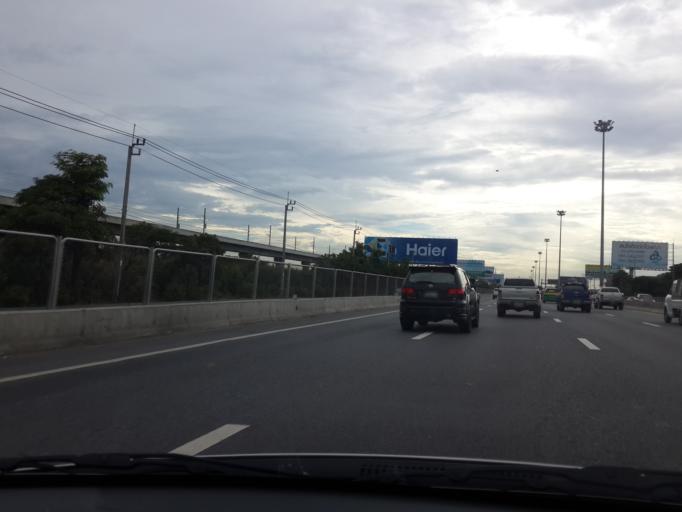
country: TH
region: Bangkok
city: Suan Luang
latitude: 13.7345
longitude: 100.6853
